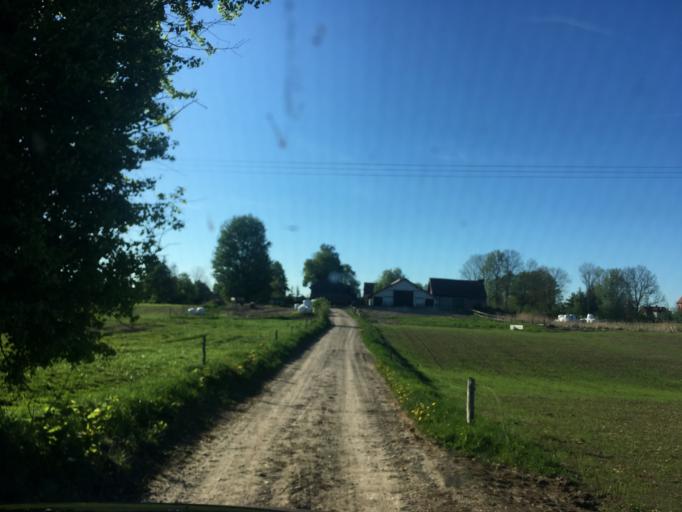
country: PL
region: Warmian-Masurian Voivodeship
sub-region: Powiat piski
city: Ruciane-Nida
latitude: 53.6615
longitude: 21.4786
